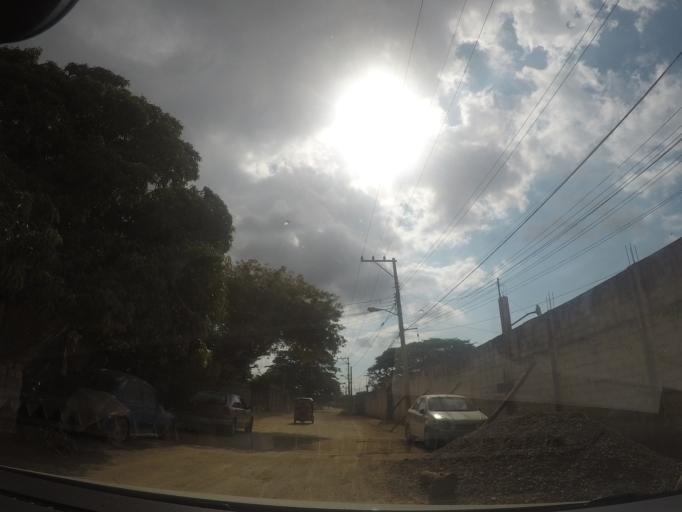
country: MX
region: Oaxaca
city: Juchitan de Zaragoza
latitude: 16.4291
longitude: -95.0335
